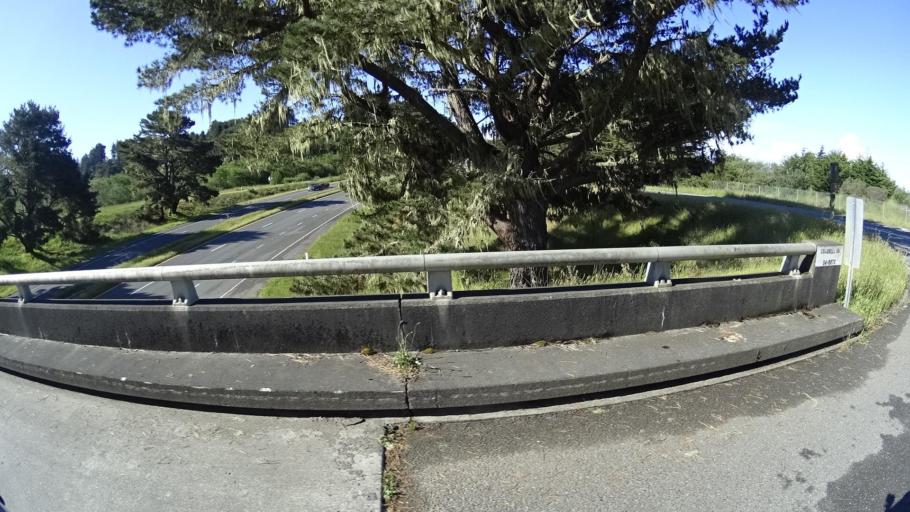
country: US
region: California
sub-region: Humboldt County
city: Westhaven-Moonstone
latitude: 41.0138
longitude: -124.1087
